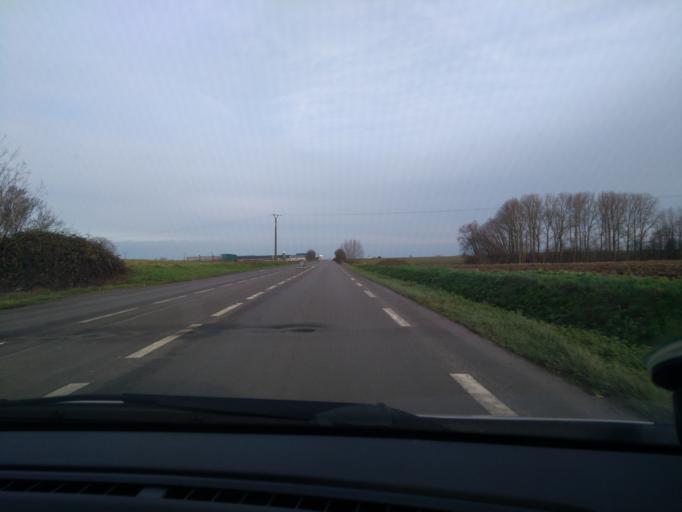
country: FR
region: Nord-Pas-de-Calais
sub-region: Departement du Nord
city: Maubeuge
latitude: 50.3195
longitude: 3.9764
